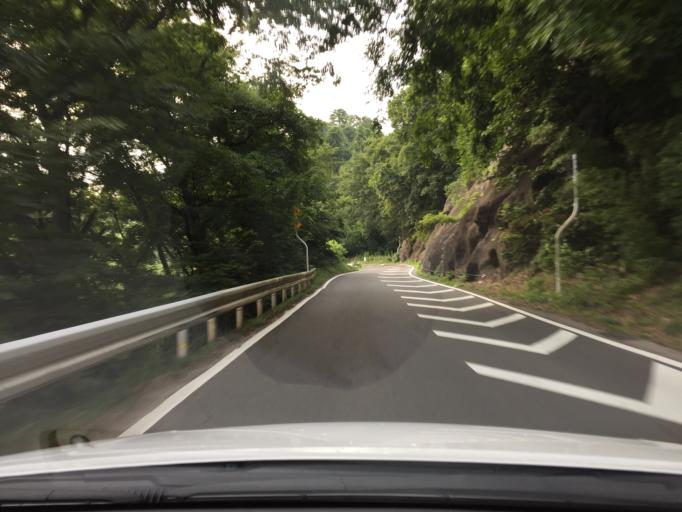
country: JP
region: Fukushima
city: Fukushima-shi
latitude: 37.7189
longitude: 140.4970
